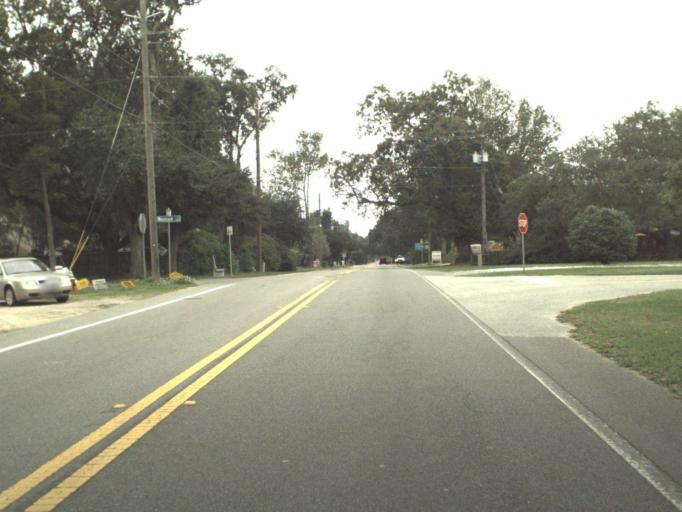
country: US
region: Florida
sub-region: Escambia County
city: Ferry Pass
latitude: 30.4965
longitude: -87.1693
